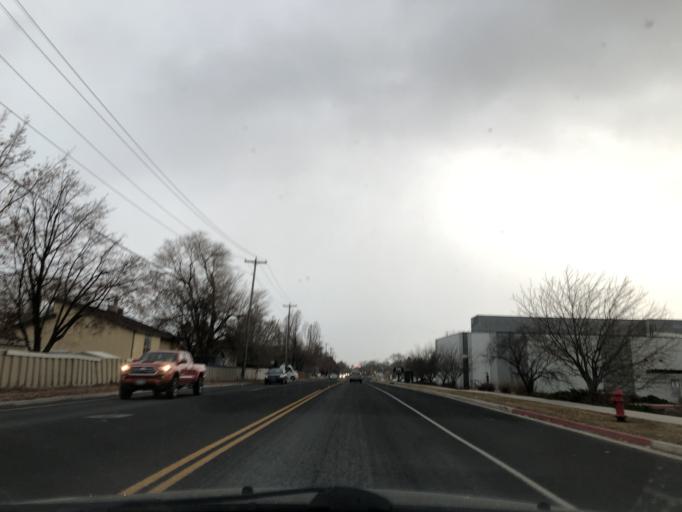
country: US
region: Utah
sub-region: Cache County
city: Logan
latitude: 41.7539
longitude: -111.8292
